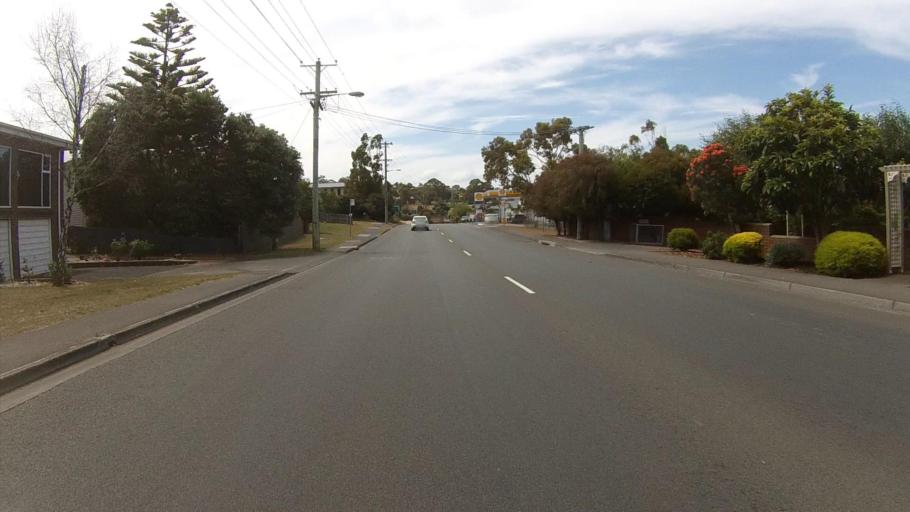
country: AU
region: Tasmania
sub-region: Kingborough
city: Blackmans Bay
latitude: -43.0010
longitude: 147.3199
